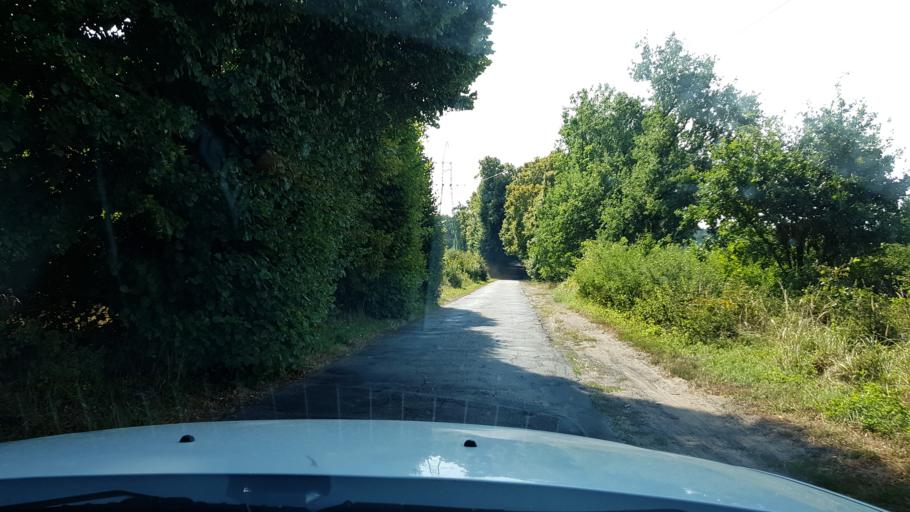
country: PL
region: West Pomeranian Voivodeship
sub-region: Powiat gryfinski
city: Chojna
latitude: 52.9492
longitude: 14.5097
